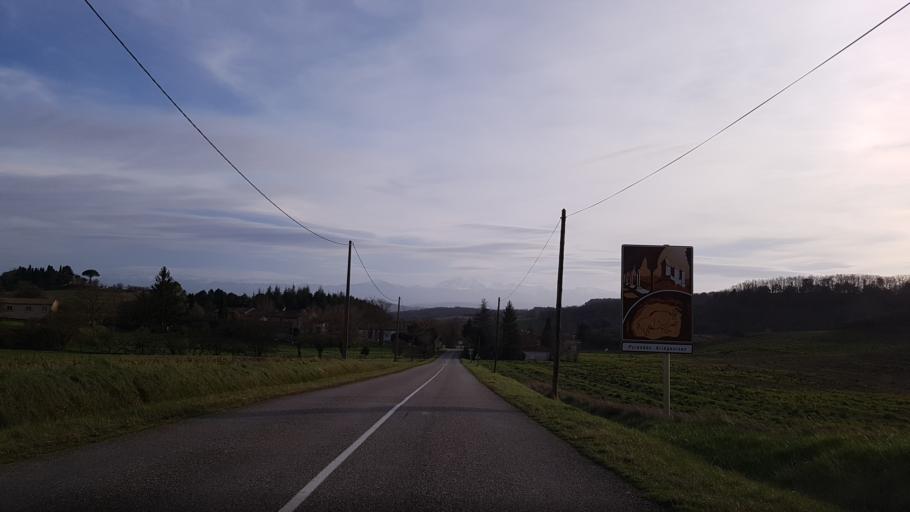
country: FR
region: Midi-Pyrenees
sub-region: Departement de l'Ariege
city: Mirepoix
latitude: 43.1315
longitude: 1.9150
